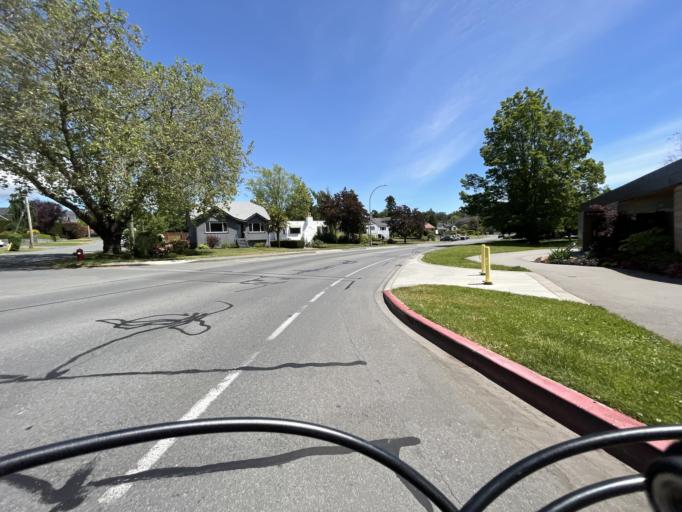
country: CA
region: British Columbia
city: Victoria
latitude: 48.4506
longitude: -123.4118
